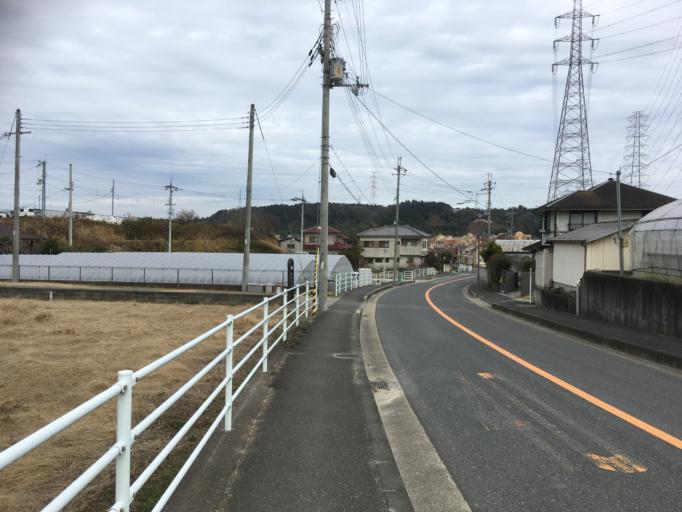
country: JP
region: Nara
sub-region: Ikoma-shi
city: Ikoma
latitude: 34.7145
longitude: 135.6970
